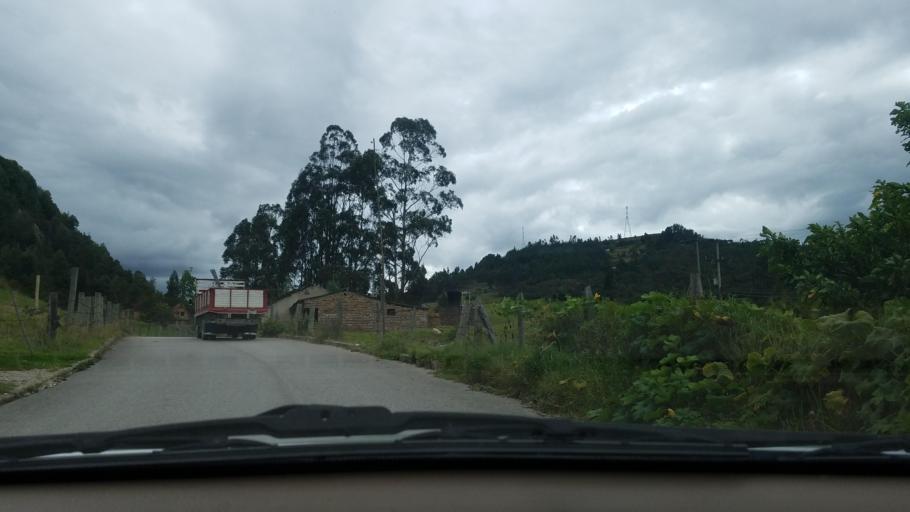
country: CO
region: Boyaca
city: Paipa
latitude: 5.7326
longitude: -73.1134
